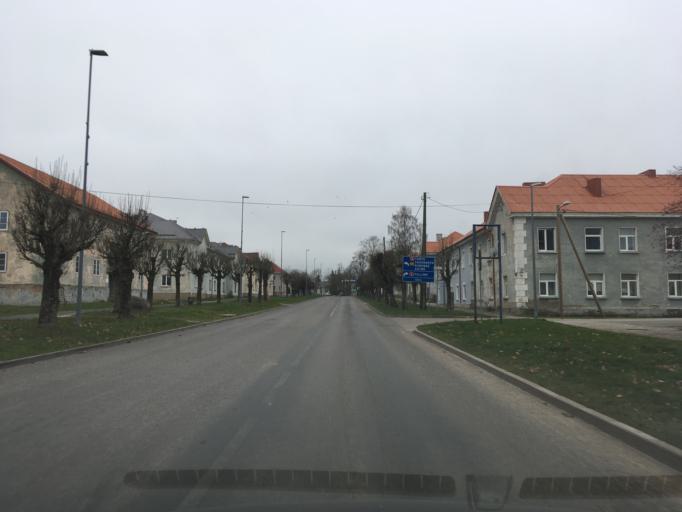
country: EE
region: Ida-Virumaa
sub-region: Johvi vald
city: Johvi
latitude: 59.3620
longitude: 27.4088
